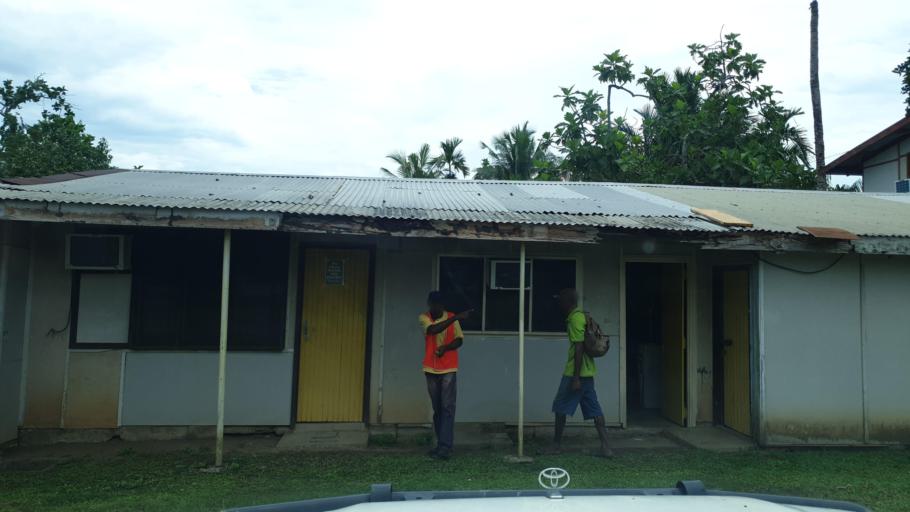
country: PG
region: Gulf
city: Kerema
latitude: -7.9608
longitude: 145.7714
